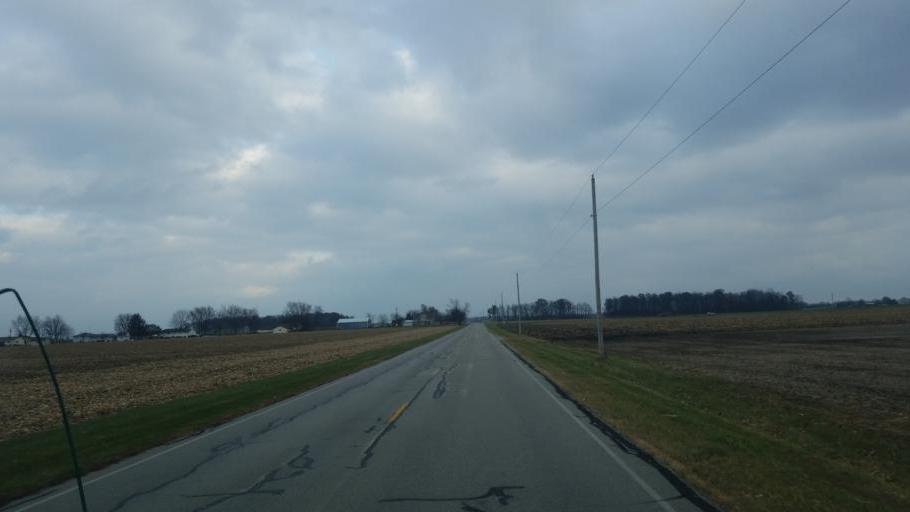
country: US
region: Ohio
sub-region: Mercer County
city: Coldwater
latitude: 40.5089
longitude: -84.6339
